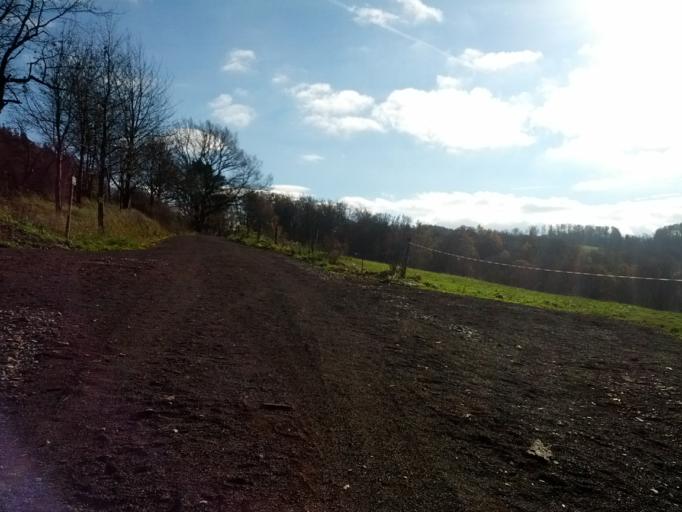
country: DE
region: Thuringia
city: Krauthausen
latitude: 51.0004
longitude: 10.2257
